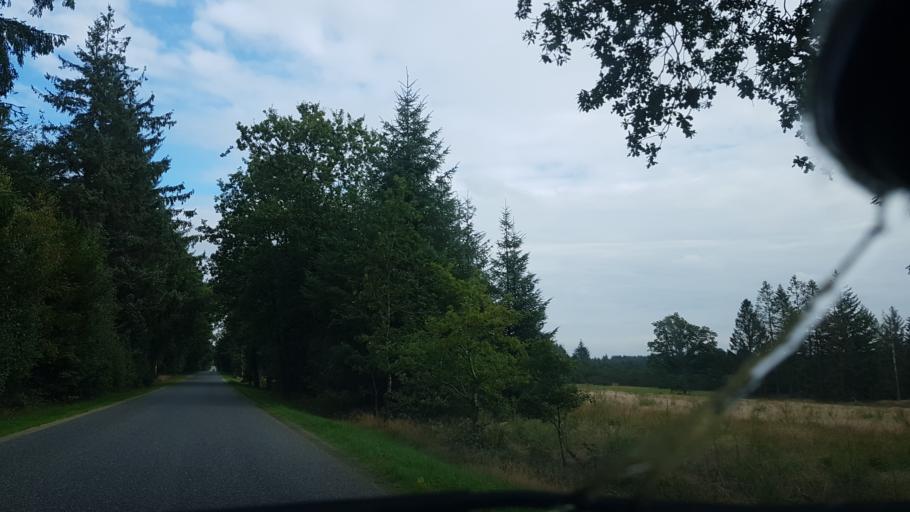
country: DK
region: South Denmark
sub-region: Vejen Kommune
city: Brorup
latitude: 55.6149
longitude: 9.0154
